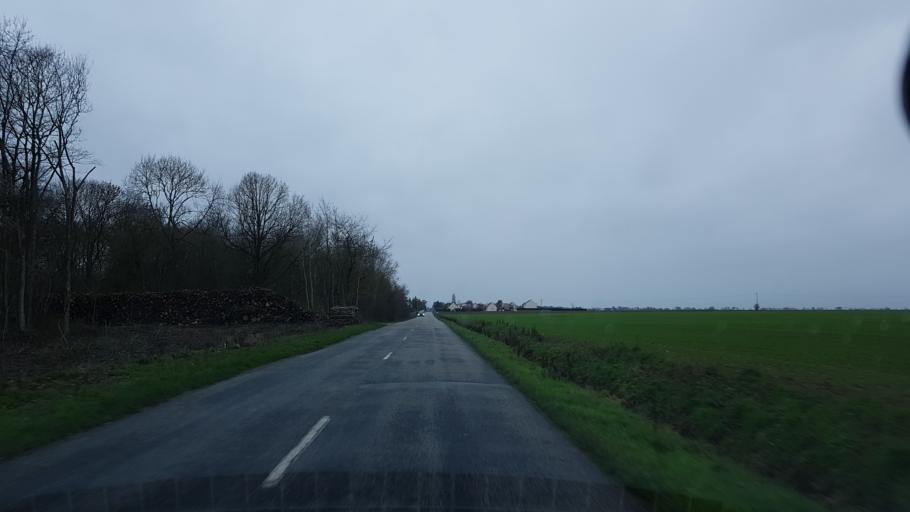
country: FR
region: Ile-de-France
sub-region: Departement de l'Essonne
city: Briis-sous-Forges
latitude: 48.6433
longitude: 2.1173
